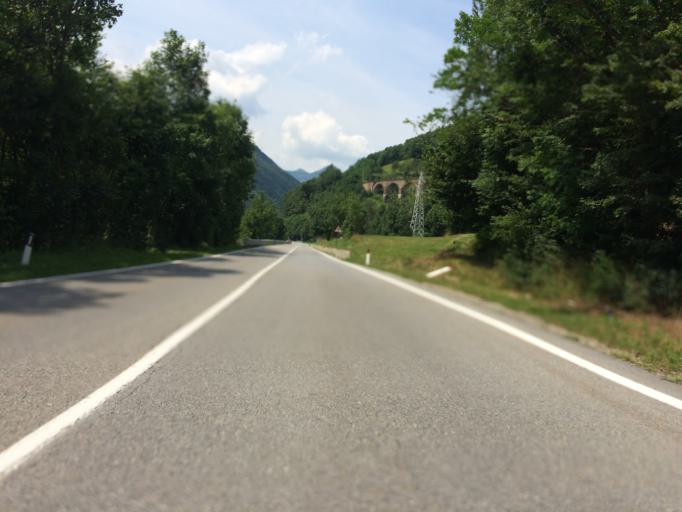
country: IT
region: Piedmont
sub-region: Provincia di Cuneo
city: Vernante
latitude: 44.2351
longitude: 7.5467
